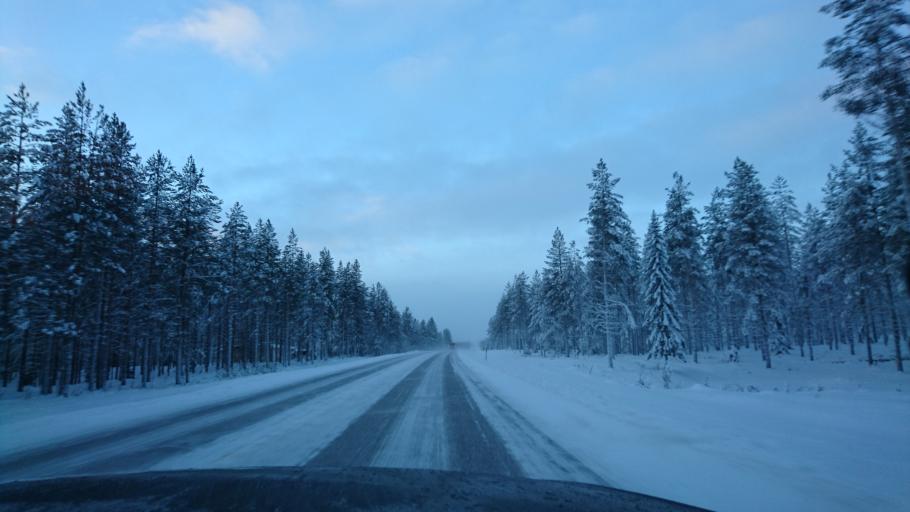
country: FI
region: Northern Ostrobothnia
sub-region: Koillismaa
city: Taivalkoski
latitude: 65.4908
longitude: 27.8981
